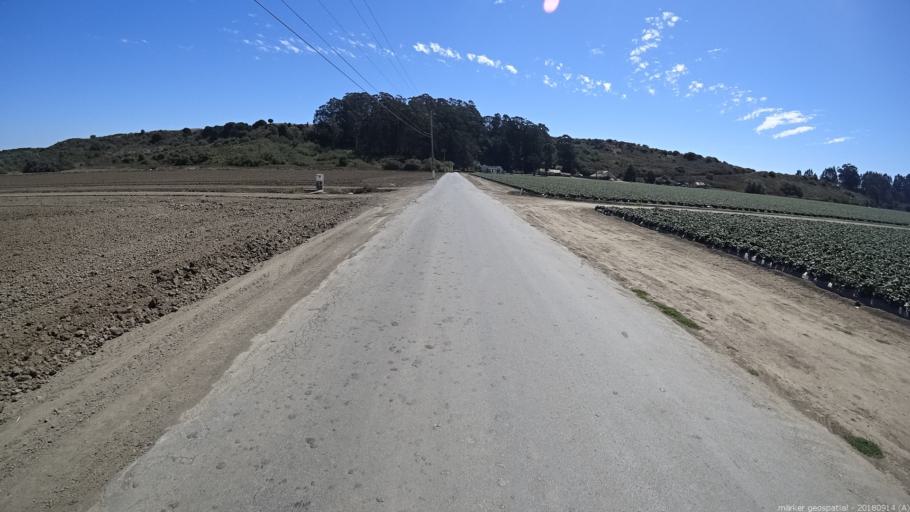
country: US
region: California
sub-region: Santa Cruz County
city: Watsonville
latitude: 36.8729
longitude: -121.7870
